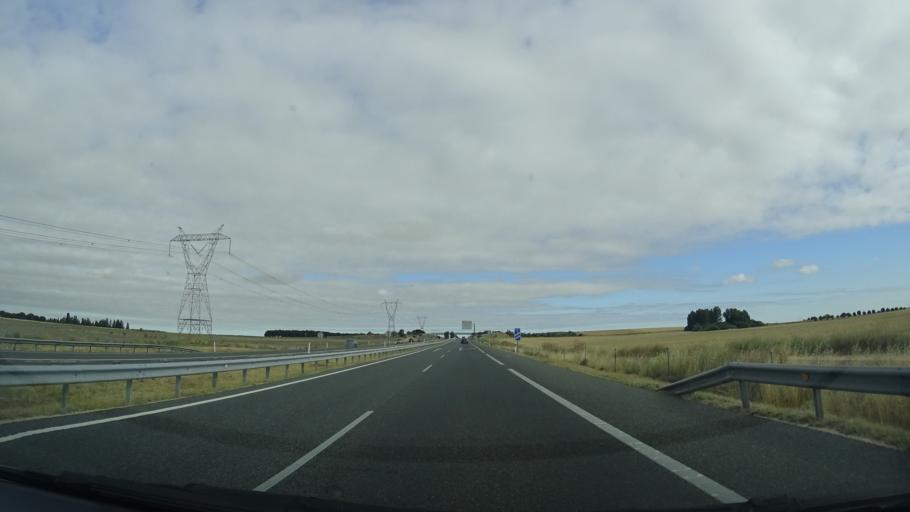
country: ES
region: Castille and Leon
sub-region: Provincia de Valladolid
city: San Pablo de la Moraleja
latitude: 41.1442
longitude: -4.7849
